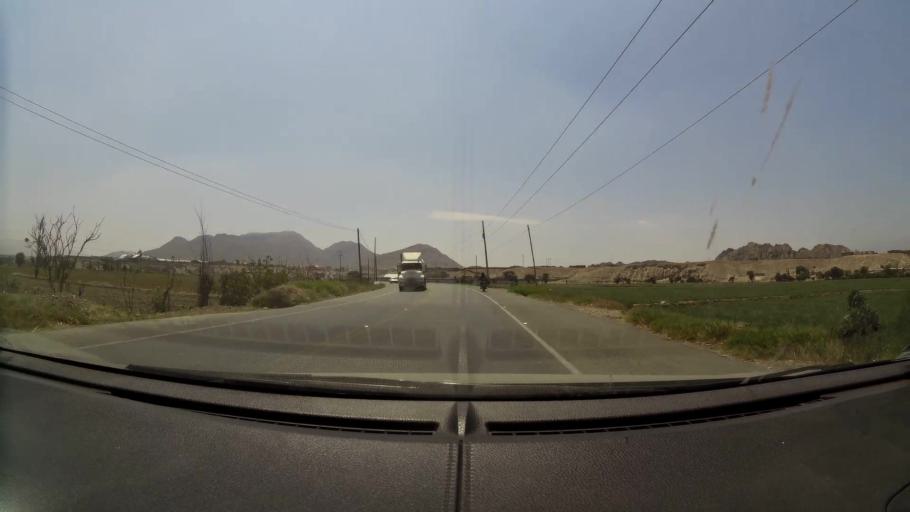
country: PE
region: La Libertad
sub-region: Provincia de Pacasmayo
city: Guadalupe
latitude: -7.3193
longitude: -79.4803
